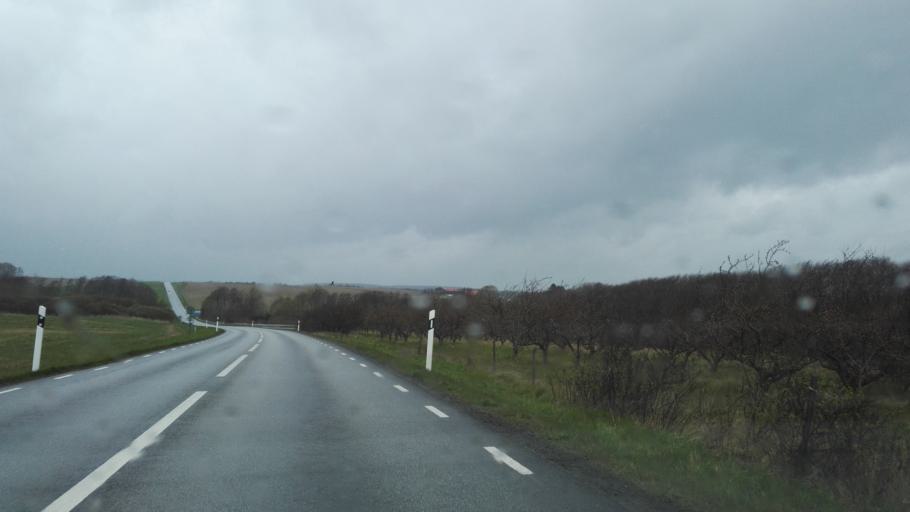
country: SE
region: Skane
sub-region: Simrishamns Kommun
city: Kivik
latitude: 55.6969
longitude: 14.2019
